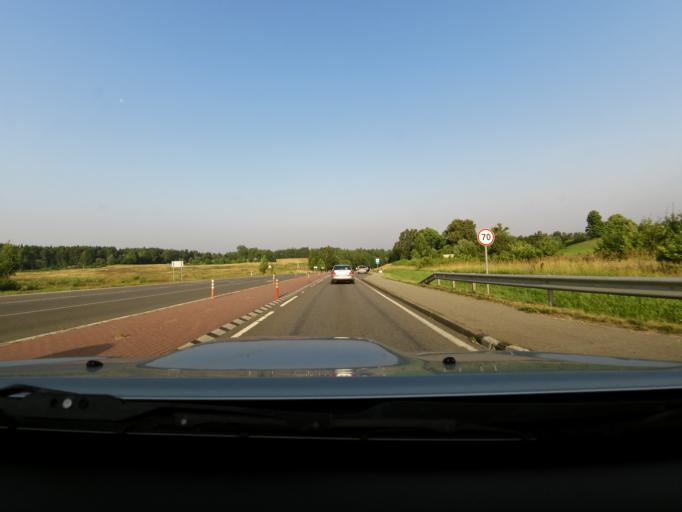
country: LT
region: Alytaus apskritis
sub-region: Alytus
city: Alytus
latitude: 54.3654
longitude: 24.1040
